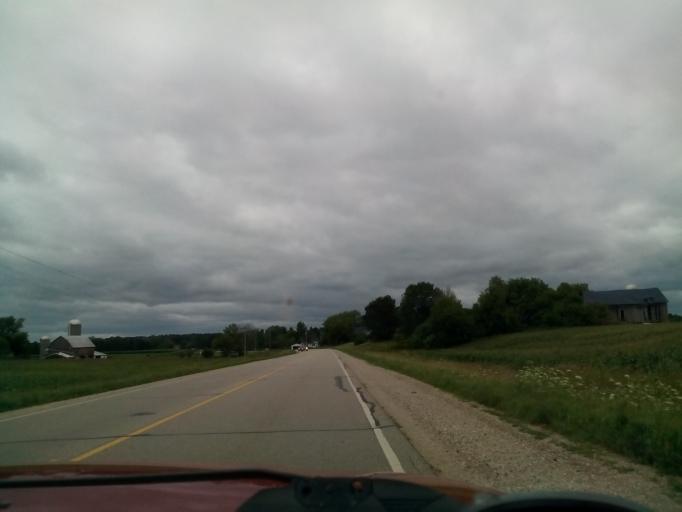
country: US
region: Wisconsin
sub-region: Oconto County
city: Gillett
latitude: 44.9998
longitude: -88.4210
